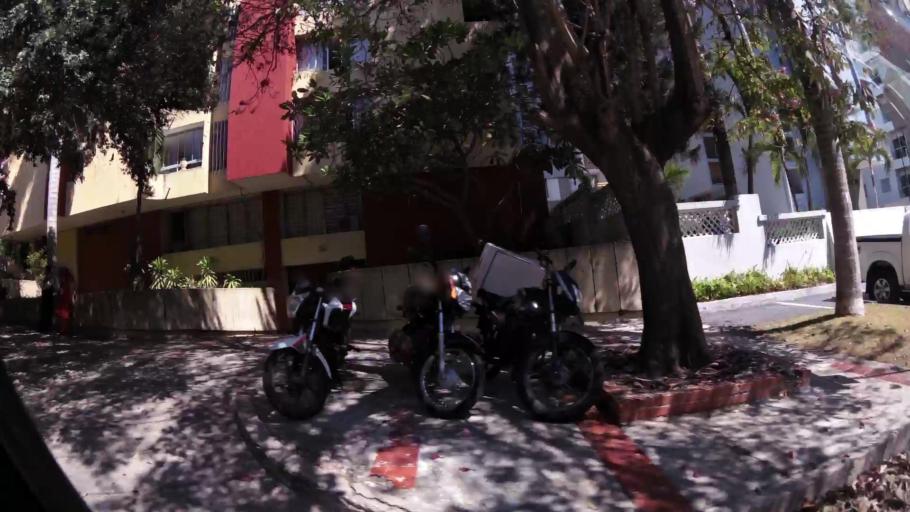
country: CO
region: Atlantico
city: Barranquilla
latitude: 11.0008
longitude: -74.8100
